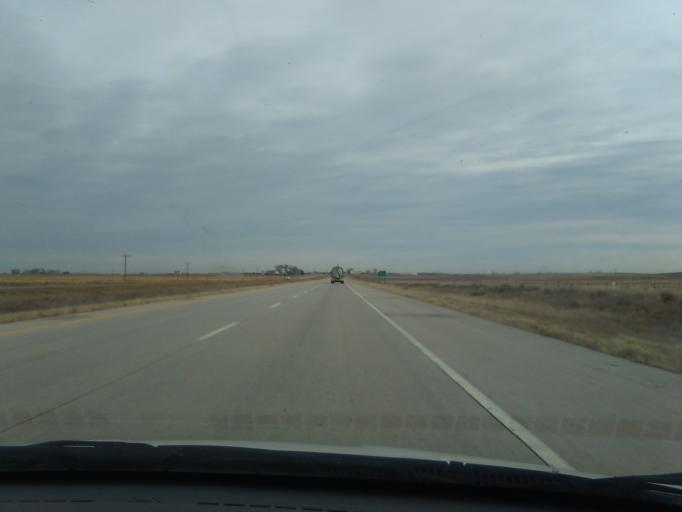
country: US
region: Colorado
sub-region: Morgan County
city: Fort Morgan
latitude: 40.2322
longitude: -104.1190
